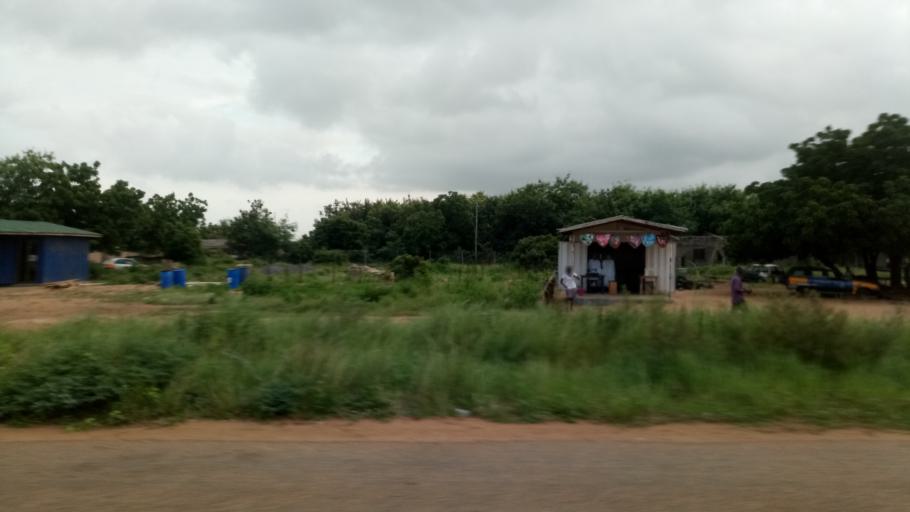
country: GH
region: Greater Accra
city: Tema
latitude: 5.8754
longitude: 0.3648
